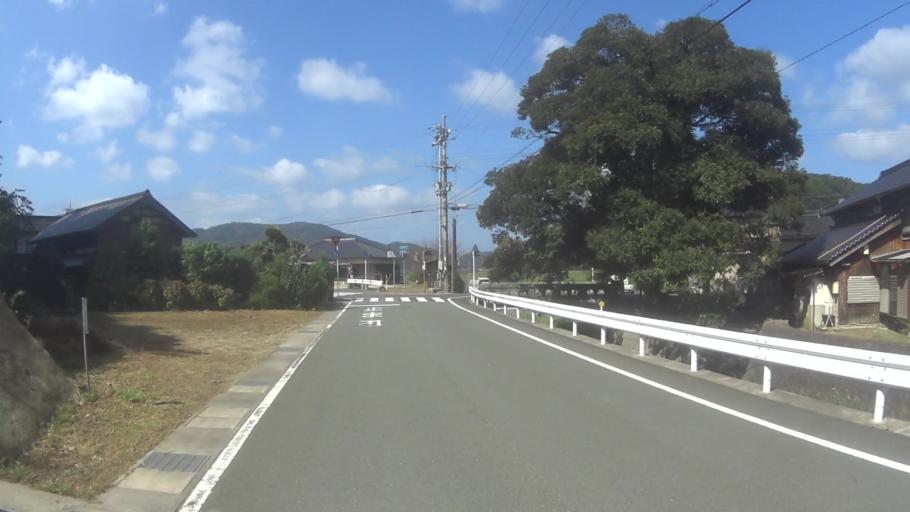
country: JP
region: Kyoto
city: Miyazu
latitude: 35.7133
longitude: 135.1142
